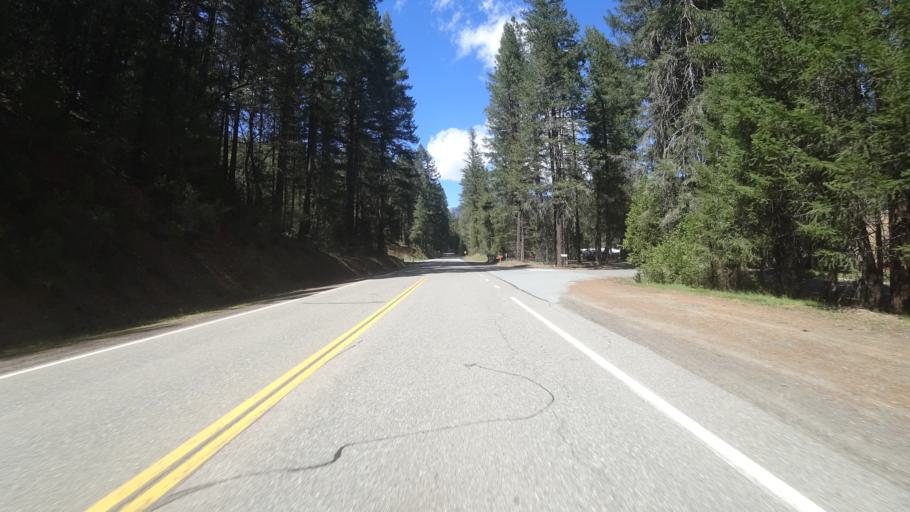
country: US
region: California
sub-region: Trinity County
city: Weaverville
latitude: 40.8027
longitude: -122.8903
